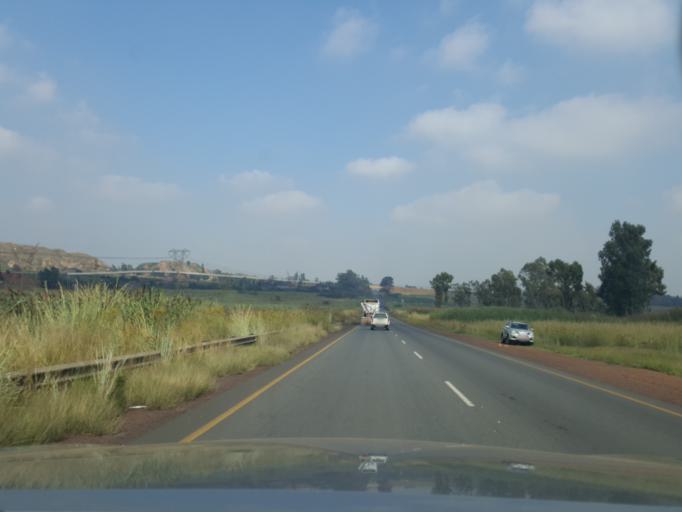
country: ZA
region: Mpumalanga
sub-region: Nkangala District Municipality
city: Witbank
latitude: -26.0140
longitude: 29.3708
